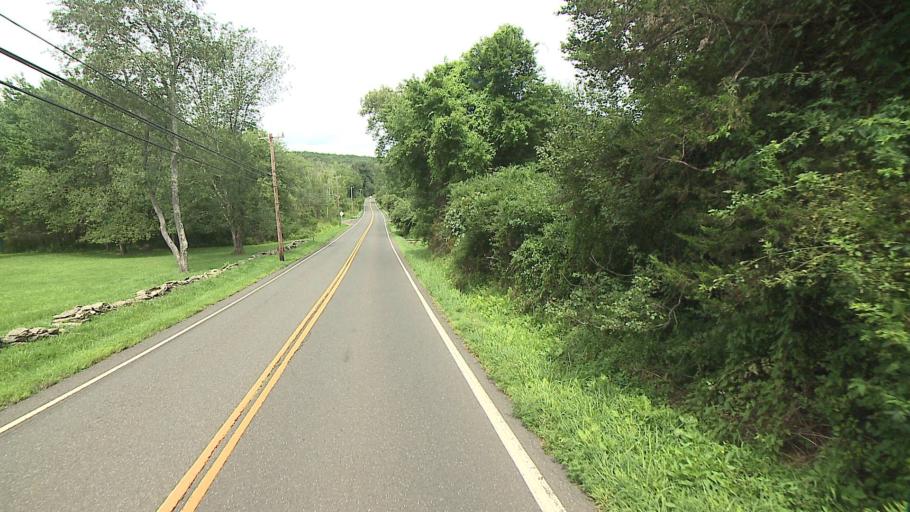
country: US
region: Connecticut
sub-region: Litchfield County
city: Woodbury
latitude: 41.5564
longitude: -73.2796
